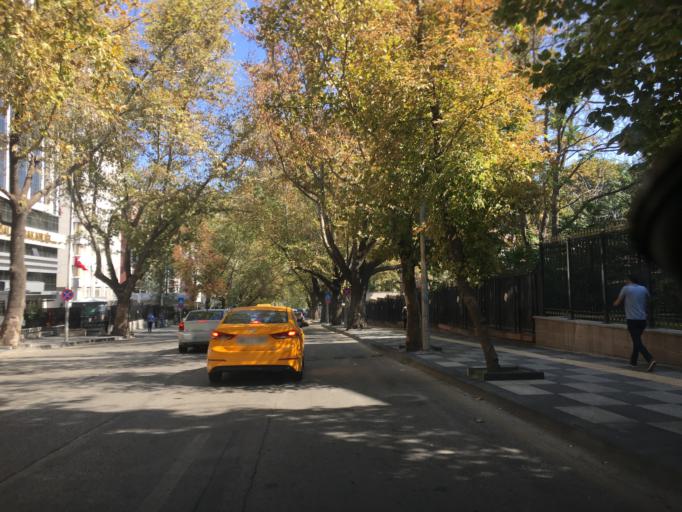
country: TR
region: Ankara
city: Ankara
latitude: 39.9175
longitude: 32.8512
